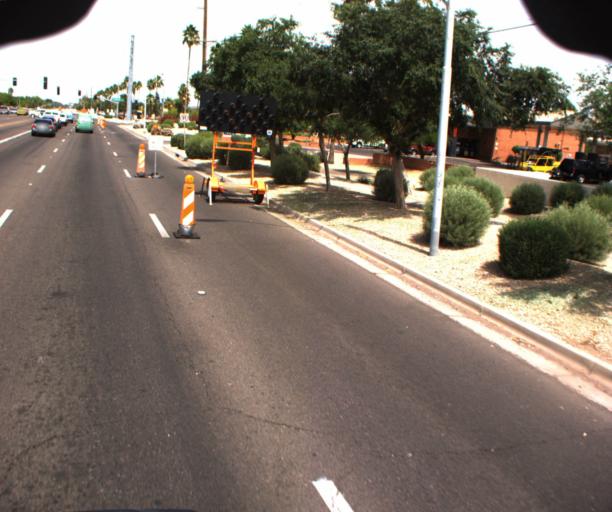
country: US
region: Arizona
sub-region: Maricopa County
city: San Carlos
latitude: 33.3630
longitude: -111.8418
